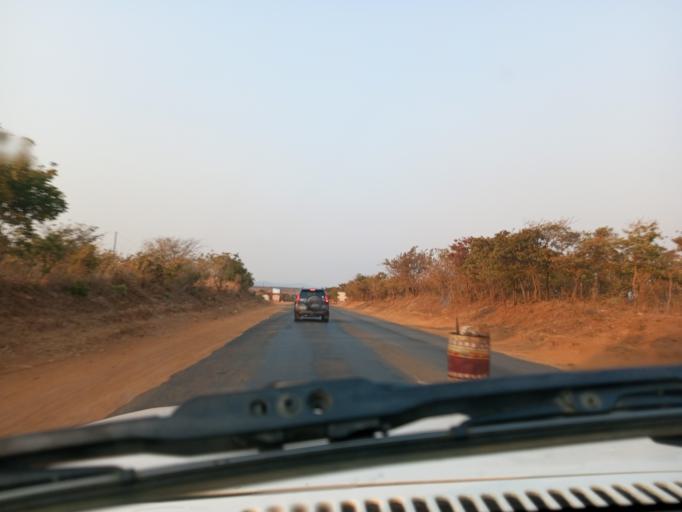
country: ZM
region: Northern
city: Mpika
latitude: -11.8925
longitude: 31.4182
